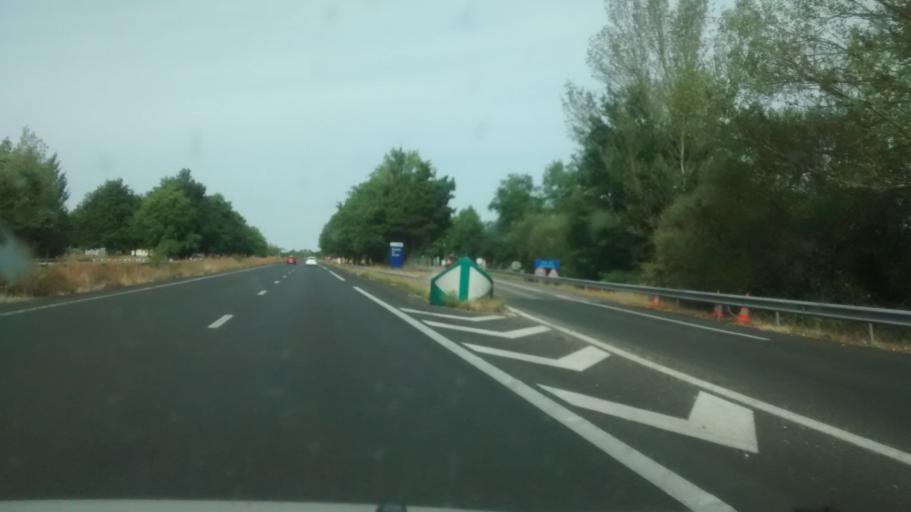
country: FR
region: Aquitaine
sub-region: Departement du Lot-et-Garonne
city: Meilhan-sur-Garonne
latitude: 44.4744
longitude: 0.0409
